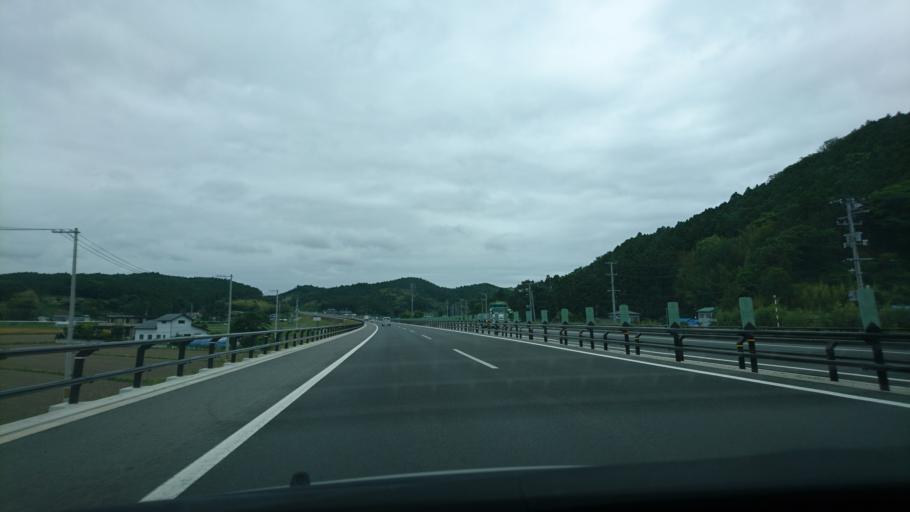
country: JP
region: Miyagi
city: Ishinomaki
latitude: 38.5257
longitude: 141.2872
